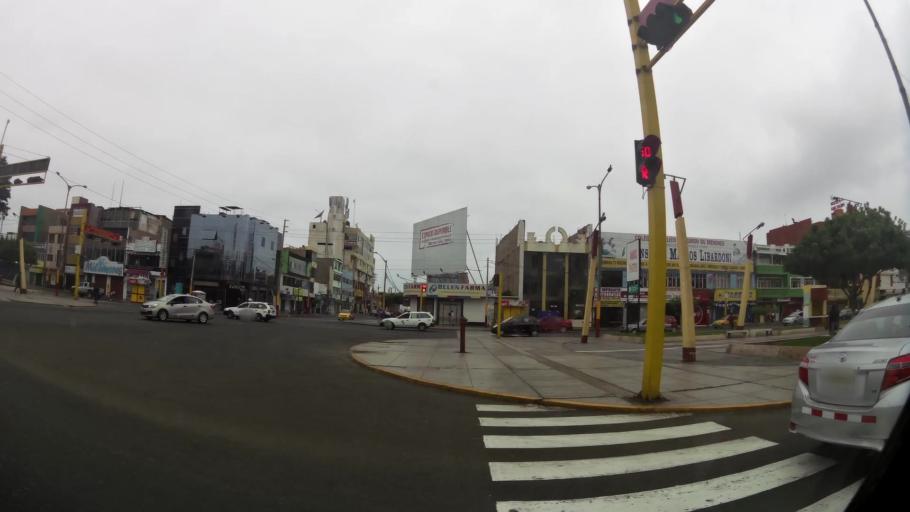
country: PE
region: Ancash
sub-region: Provincia de Santa
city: Chimbote
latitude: -9.0755
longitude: -78.5923
